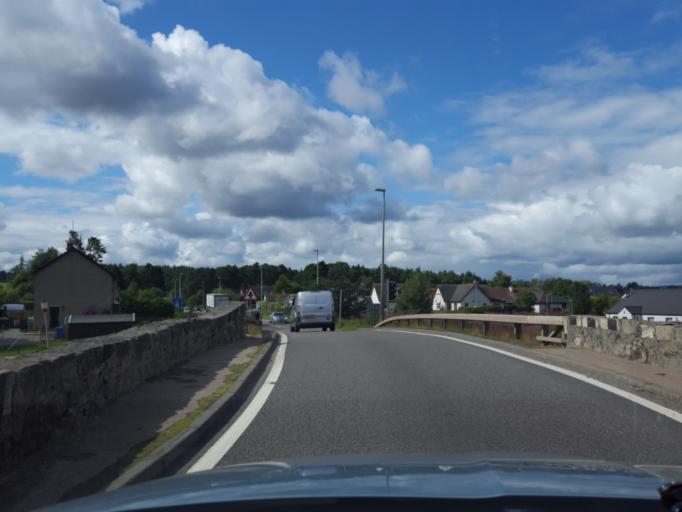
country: GB
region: Scotland
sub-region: Highland
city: Grantown on Spey
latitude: 57.3376
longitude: -3.5390
